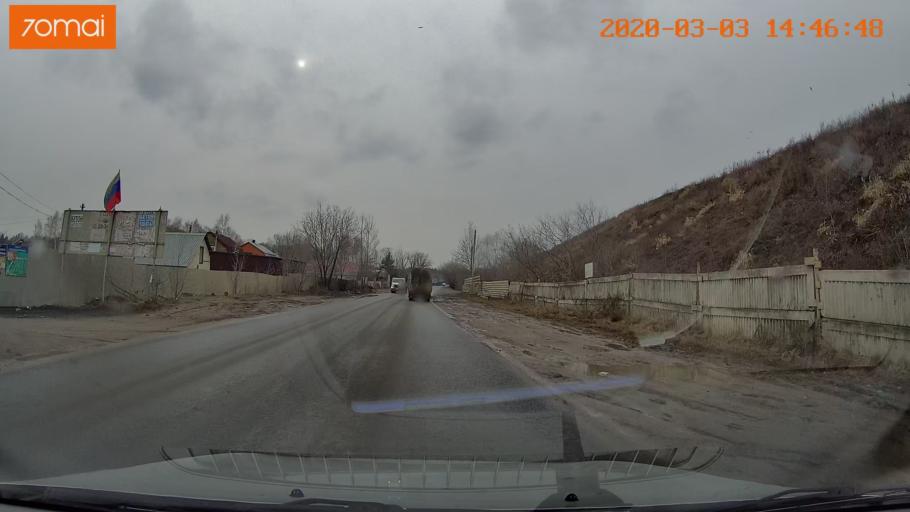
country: RU
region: Moskovskaya
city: Rodniki
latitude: 55.6954
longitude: 38.0546
